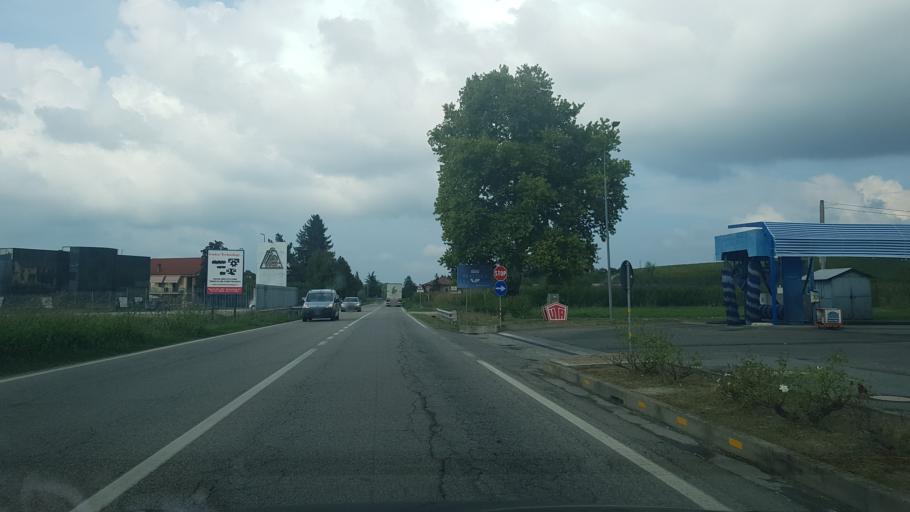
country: IT
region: Piedmont
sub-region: Provincia di Asti
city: Calamandrana
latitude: 44.7413
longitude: 8.3427
